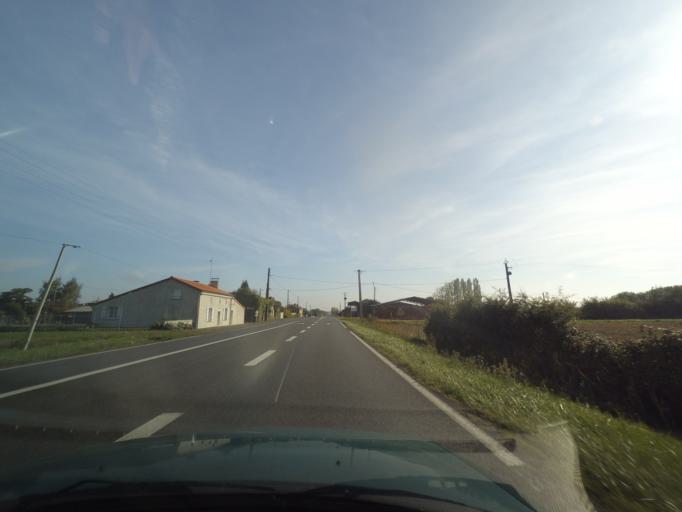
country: FR
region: Pays de la Loire
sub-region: Departement de Maine-et-Loire
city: Vihiers
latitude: 47.1501
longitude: -0.4776
